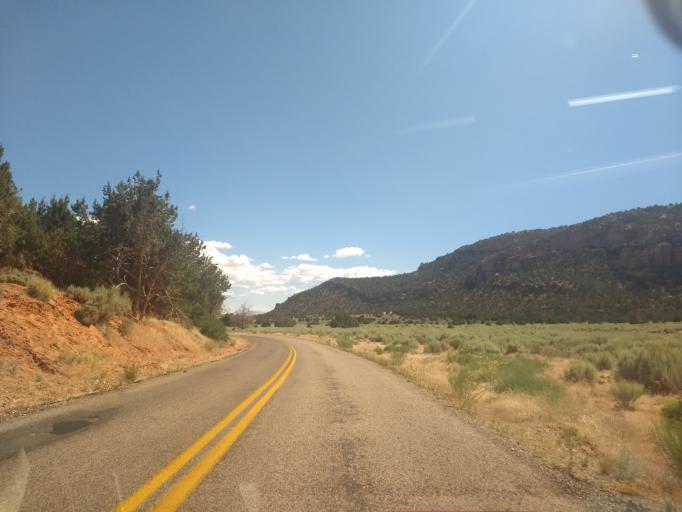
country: US
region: Utah
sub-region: Washington County
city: Hildale
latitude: 36.9716
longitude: -112.8715
